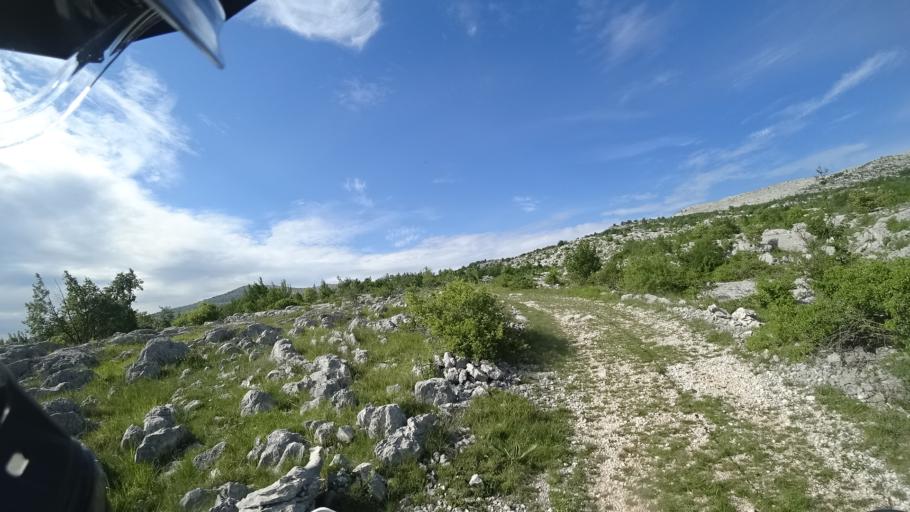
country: HR
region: Splitsko-Dalmatinska
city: Hrvace
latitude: 43.7910
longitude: 16.4345
